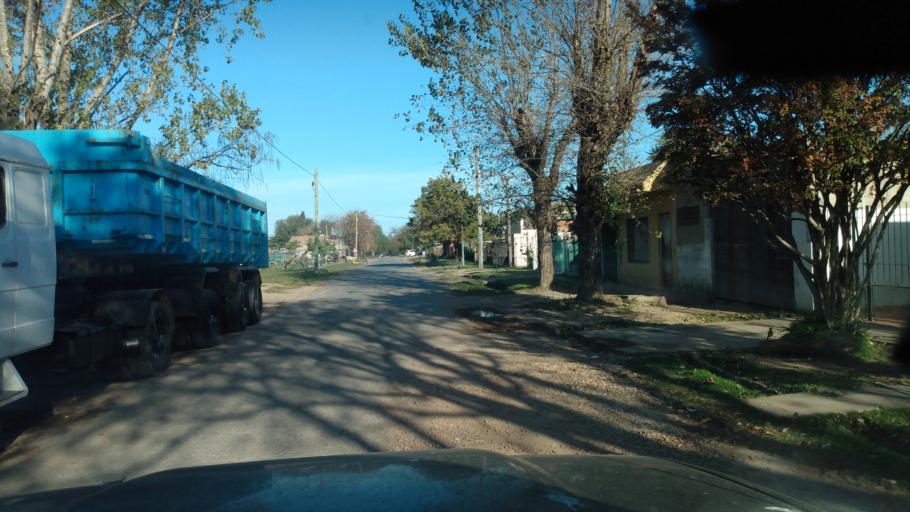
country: AR
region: Buenos Aires
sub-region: Partido de Lujan
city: Lujan
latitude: -34.5423
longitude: -59.1187
